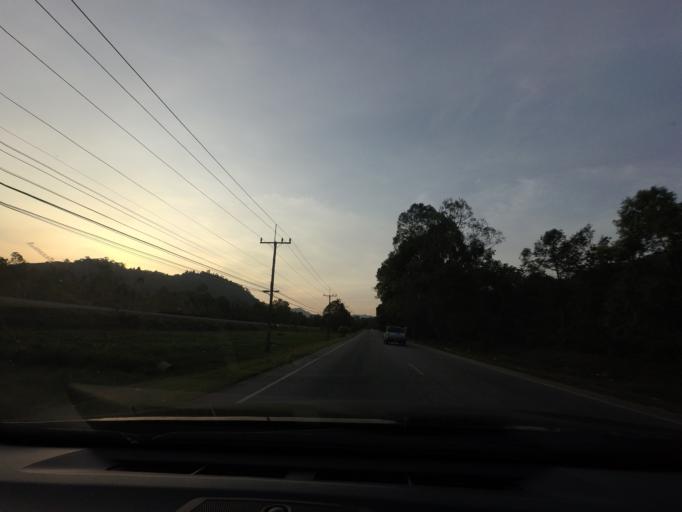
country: TH
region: Narathiwat
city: Yi-ngo
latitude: 6.3491
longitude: 101.6210
